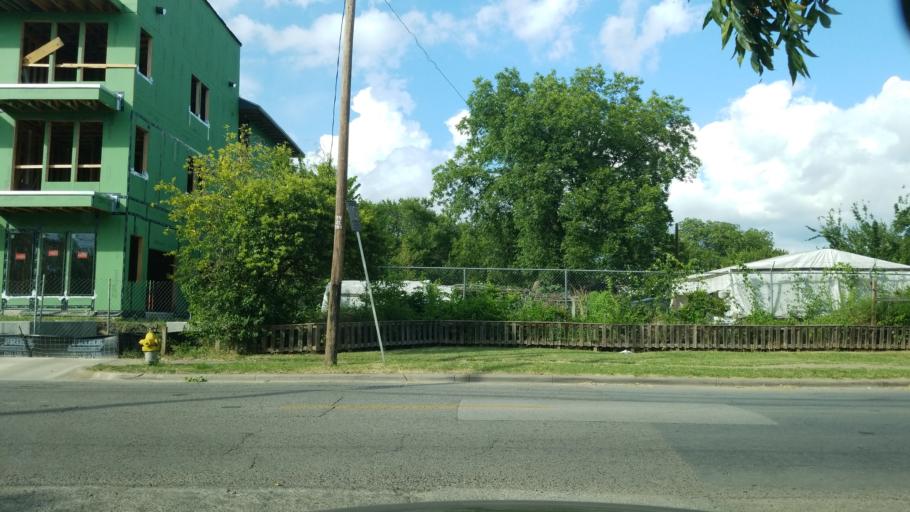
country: US
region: Texas
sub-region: Dallas County
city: Highland Park
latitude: 32.8045
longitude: -96.7744
